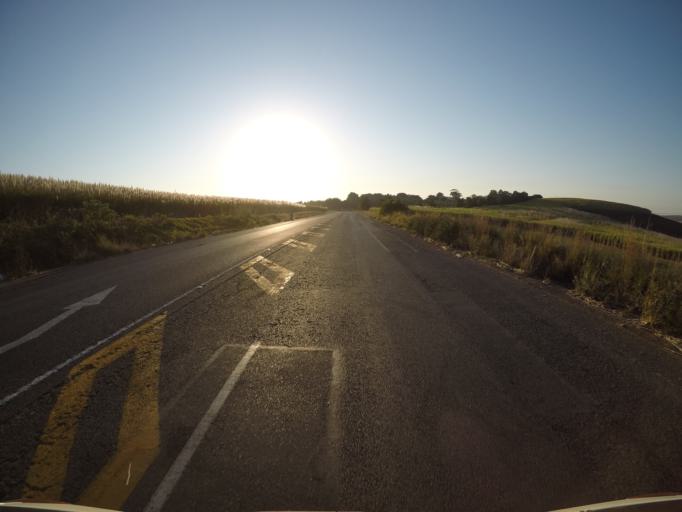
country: ZA
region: KwaZulu-Natal
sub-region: uThungulu District Municipality
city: Eshowe
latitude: -28.9492
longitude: 31.6753
